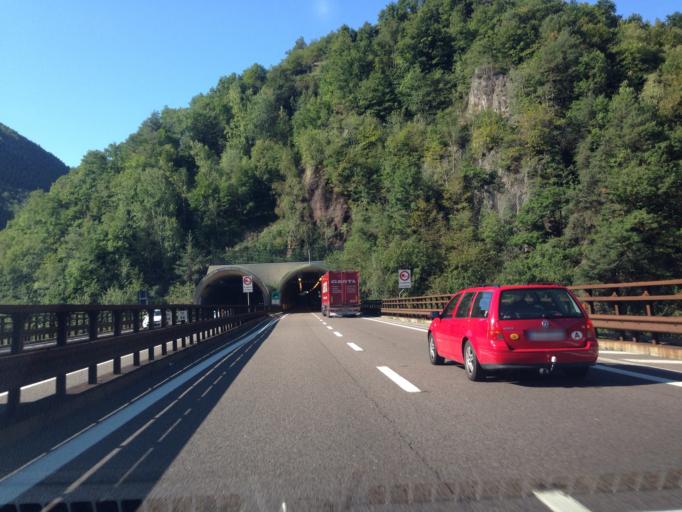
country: IT
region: Trentino-Alto Adige
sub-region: Bolzano
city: Fie Allo Sciliar
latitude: 46.5272
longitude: 11.4891
